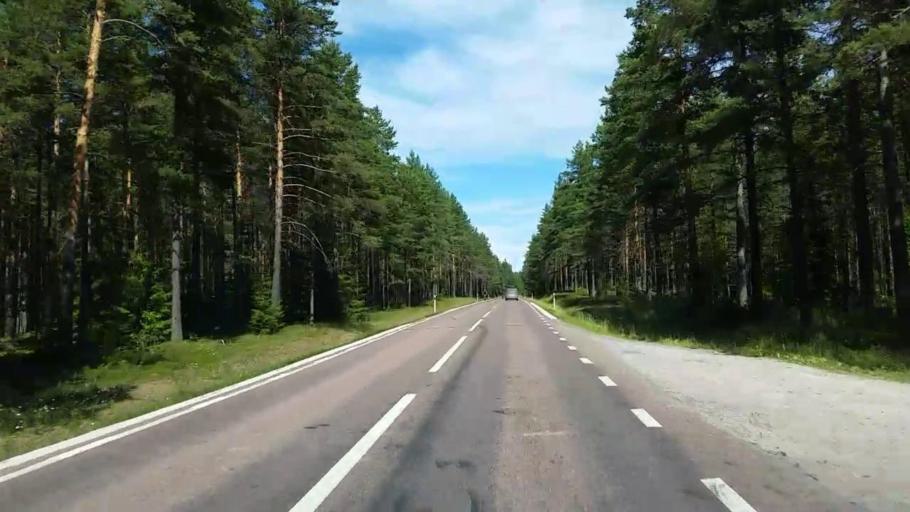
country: SE
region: Dalarna
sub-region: Rattviks Kommun
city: Raettvik
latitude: 60.9130
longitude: 15.2015
